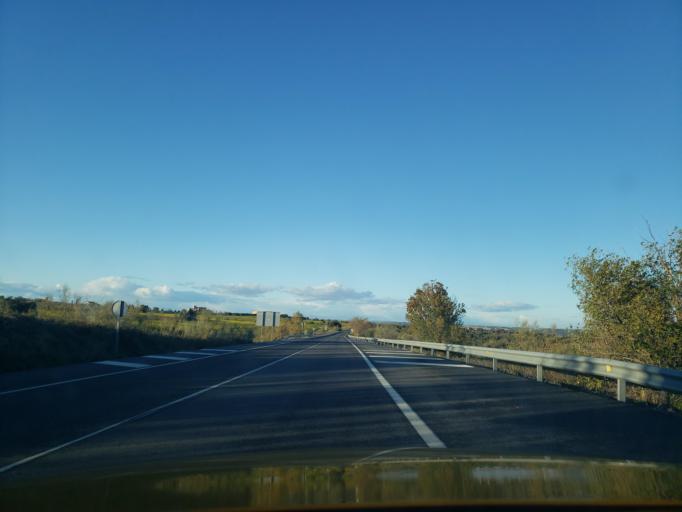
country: ES
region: Castille-La Mancha
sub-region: Province of Toledo
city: Cobisa
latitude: 39.8288
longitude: -4.0179
